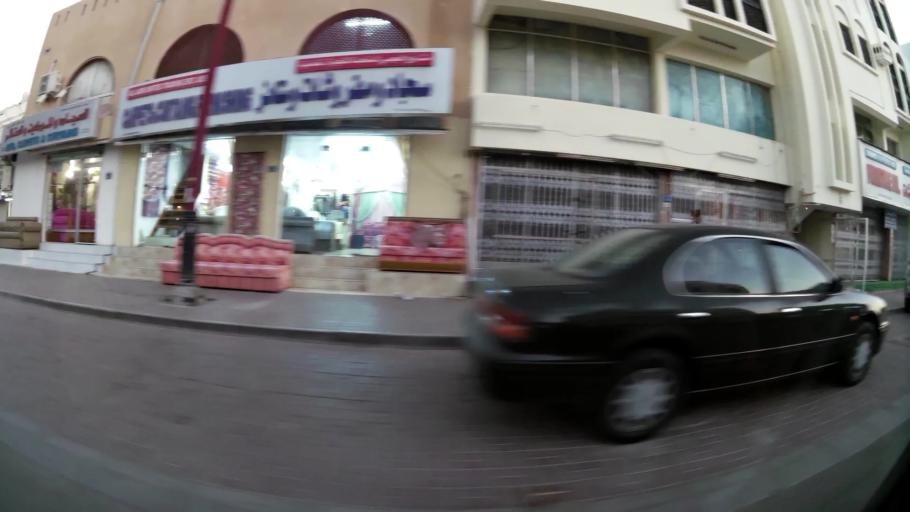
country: OM
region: Muhafazat Masqat
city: As Sib al Jadidah
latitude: 23.6840
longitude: 58.1811
